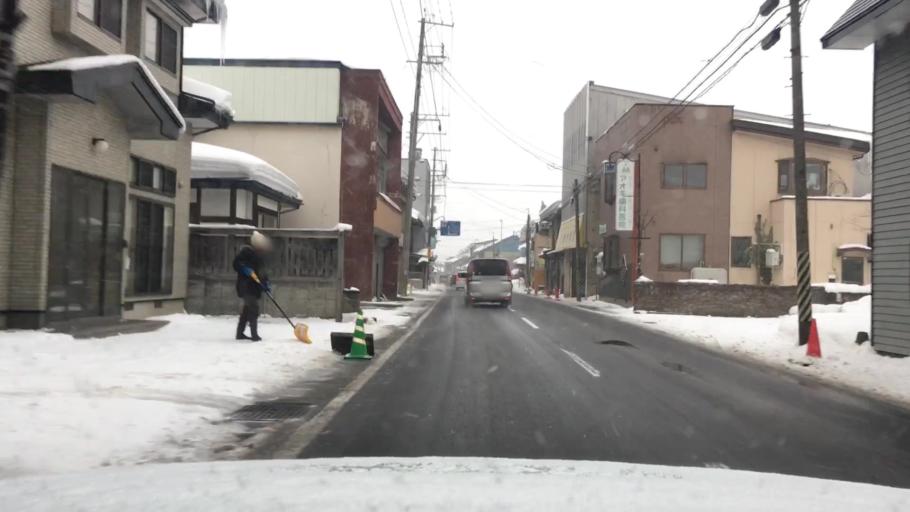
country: JP
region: Iwate
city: Ichinohe
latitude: 40.0990
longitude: 141.0479
